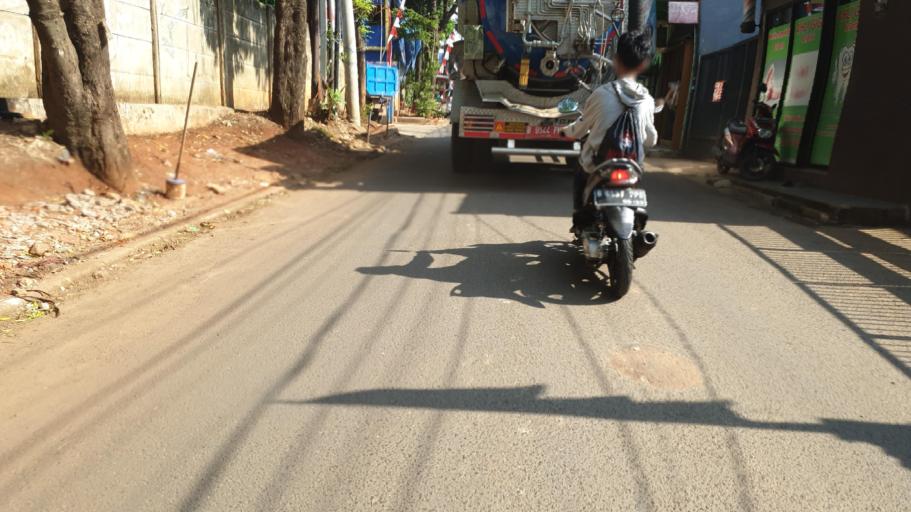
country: ID
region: Jakarta Raya
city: Jakarta
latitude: -6.2898
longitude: 106.8367
